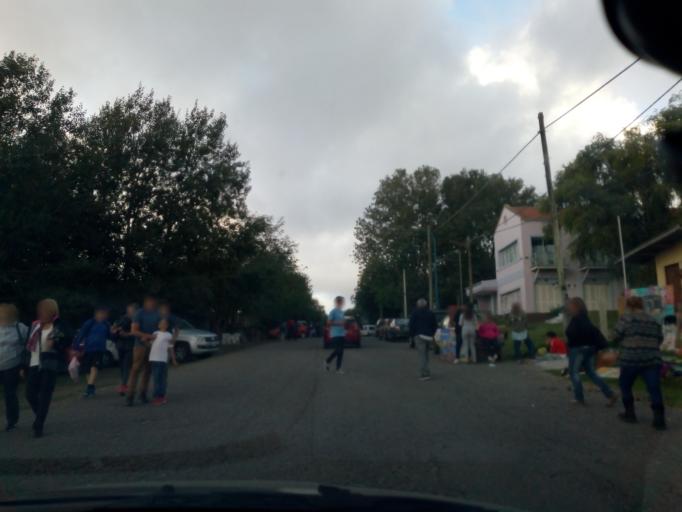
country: AR
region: Buenos Aires
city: Mar del Plata
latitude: -37.9457
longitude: -57.7798
